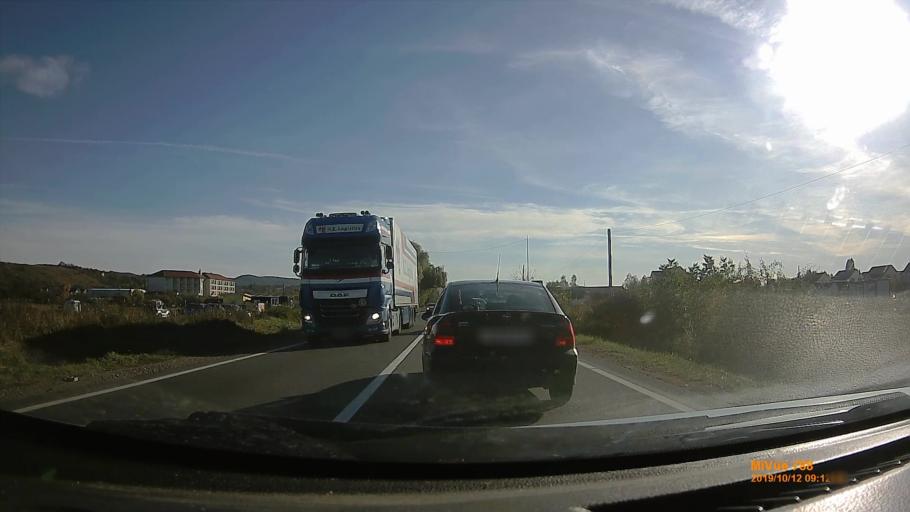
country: RO
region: Bihor
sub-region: Comuna Astileu
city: Astileu
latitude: 47.0592
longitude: 22.3796
